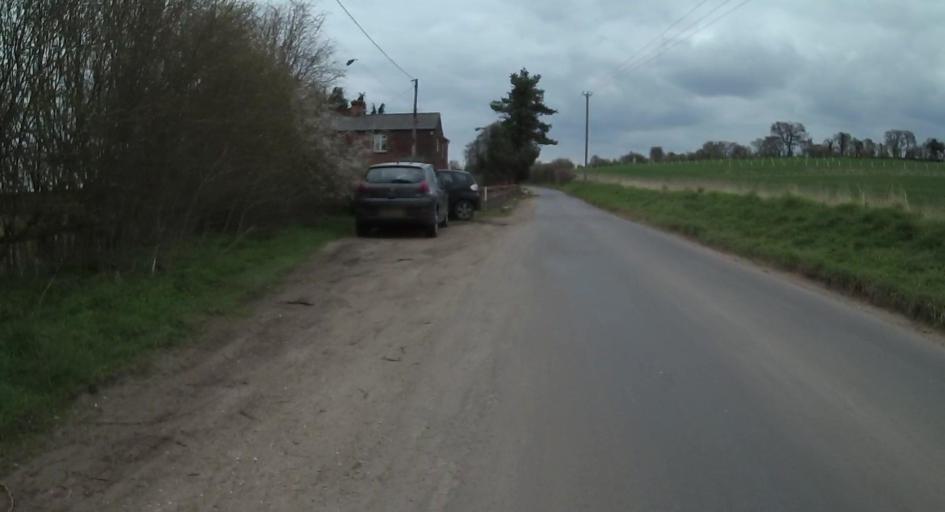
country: GB
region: England
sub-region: Hampshire
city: Odiham
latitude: 51.2409
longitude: -0.9720
